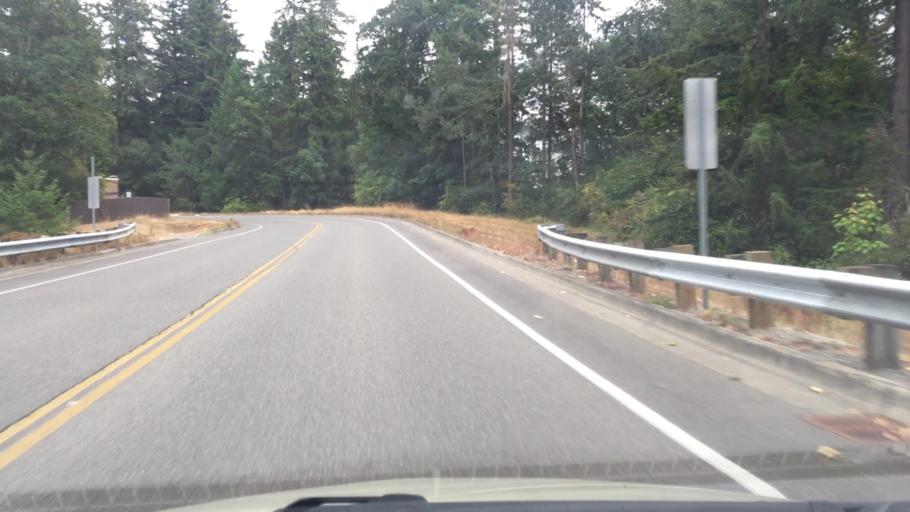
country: US
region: Washington
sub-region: Pierce County
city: Fort Lewis
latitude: 47.1078
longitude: -122.5897
